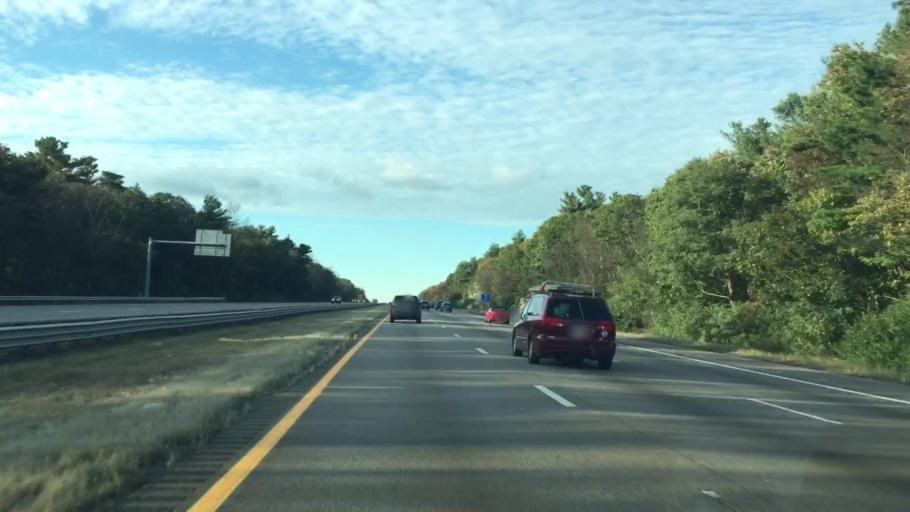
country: US
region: Massachusetts
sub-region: Norfolk County
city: Randolph
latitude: 42.1677
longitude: -71.0718
